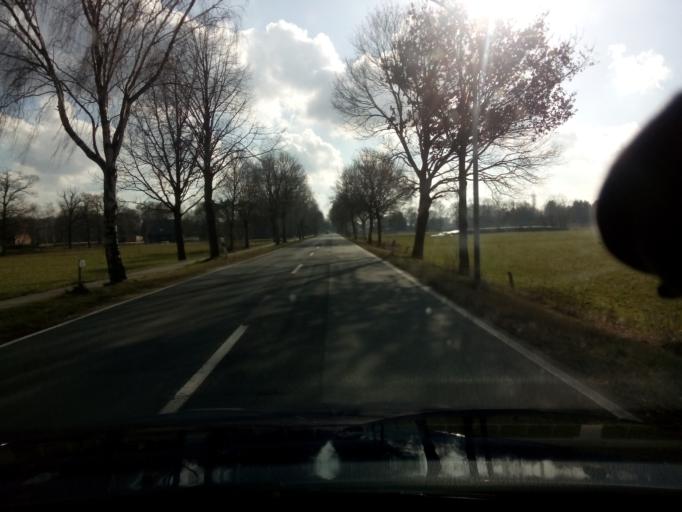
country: DE
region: Lower Saxony
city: Gnarrenburg
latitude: 53.3239
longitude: 8.9797
